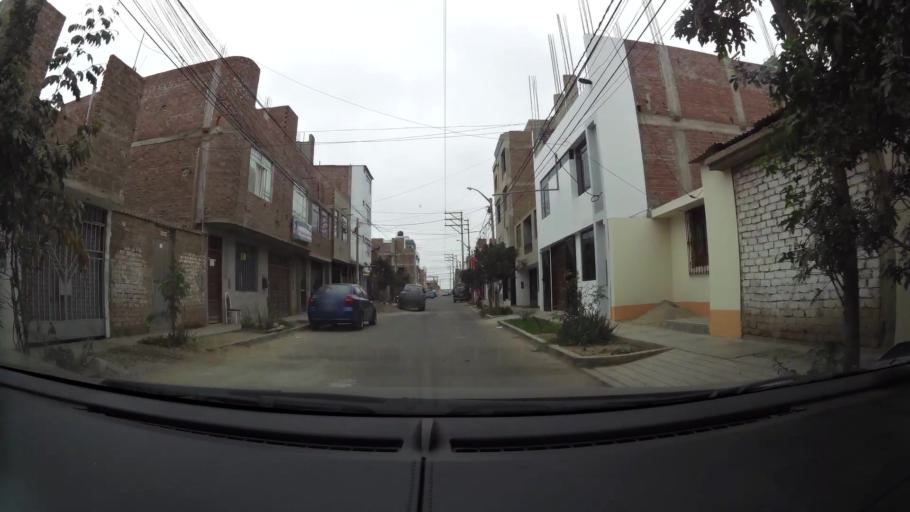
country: PE
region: La Libertad
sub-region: Provincia de Trujillo
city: Trujillo
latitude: -8.1091
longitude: -79.0456
